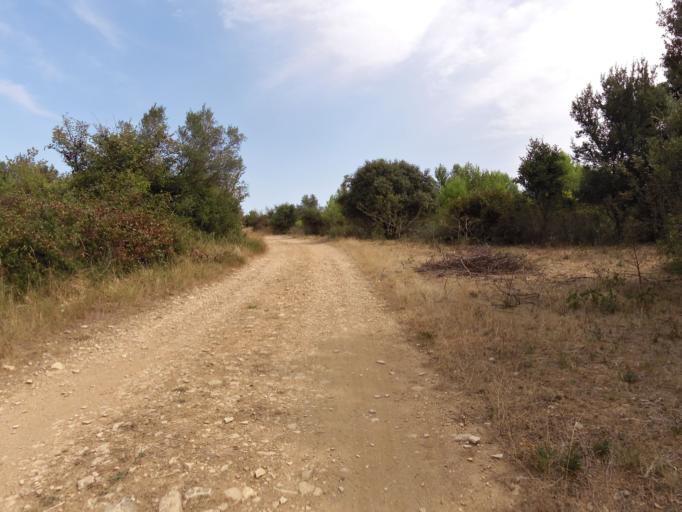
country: FR
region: Languedoc-Roussillon
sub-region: Departement du Gard
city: Congenies
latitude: 43.7605
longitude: 4.1604
